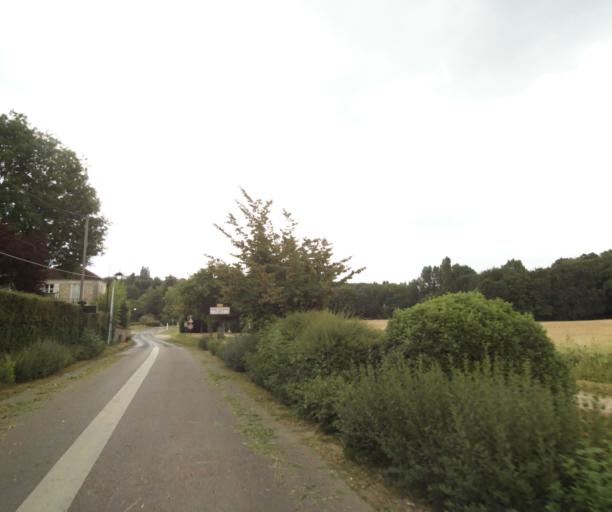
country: FR
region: Ile-de-France
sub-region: Departement de Seine-et-Marne
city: Saint-Sauveur-sur-Ecole
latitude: 48.4985
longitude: 2.5417
